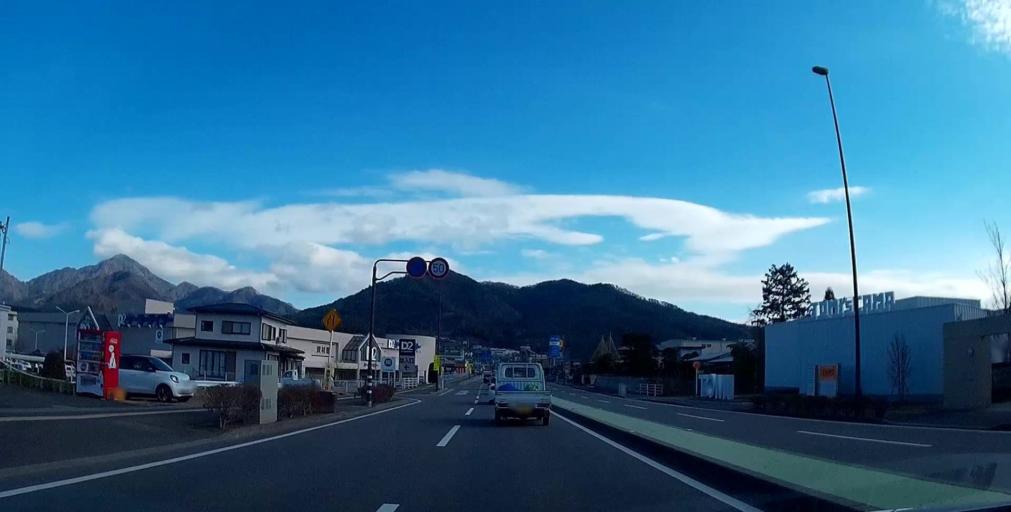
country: JP
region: Yamanashi
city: Fujikawaguchiko
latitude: 35.4827
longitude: 138.8077
